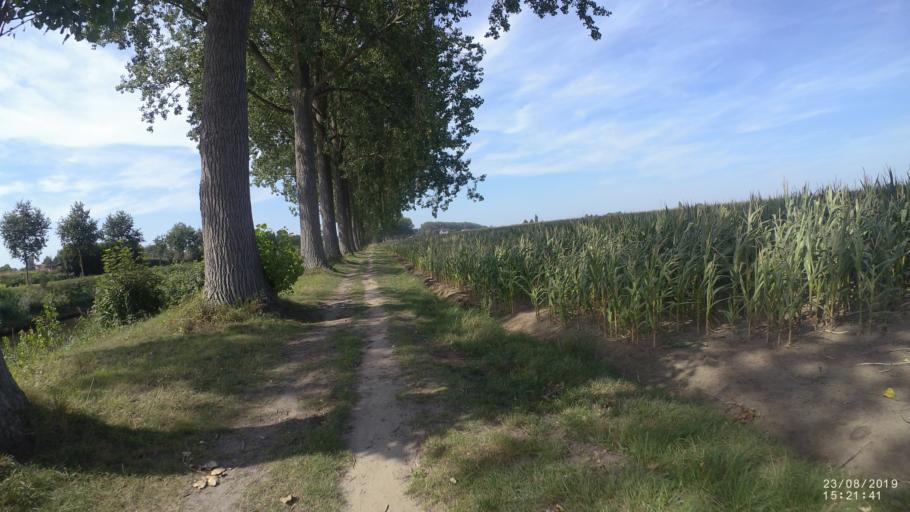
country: BE
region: Flanders
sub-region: Provincie Oost-Vlaanderen
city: Zomergem
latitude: 51.1240
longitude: 3.5692
